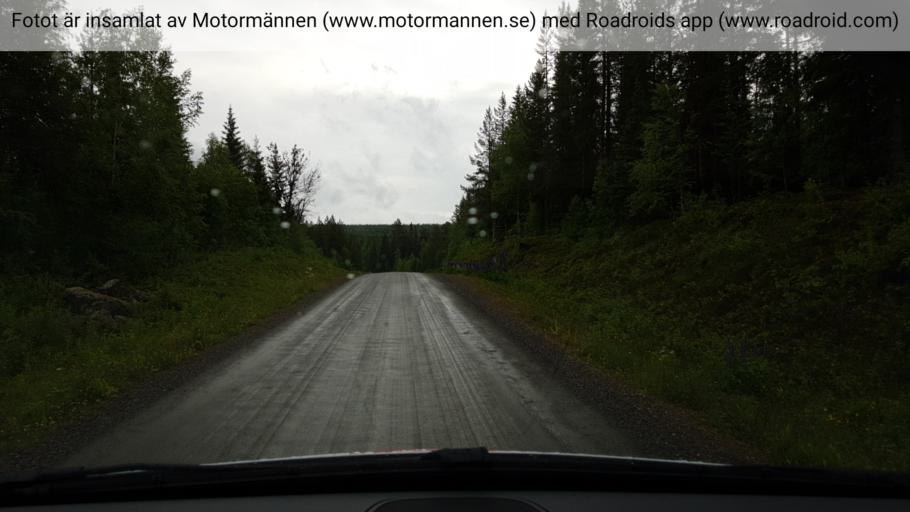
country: SE
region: Jaemtland
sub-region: Stroemsunds Kommun
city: Stroemsund
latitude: 64.2713
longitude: 15.0106
